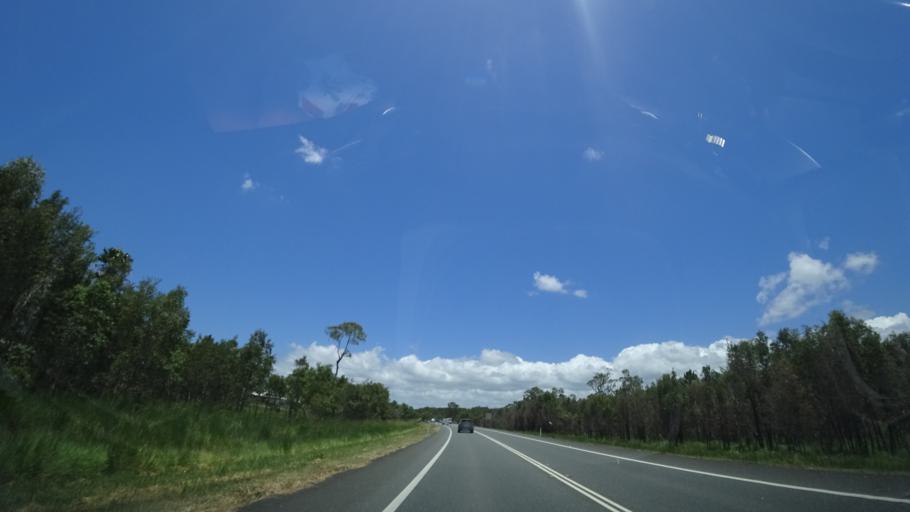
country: AU
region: Queensland
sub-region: Sunshine Coast
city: Little Mountain
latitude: -26.7722
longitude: 153.0805
